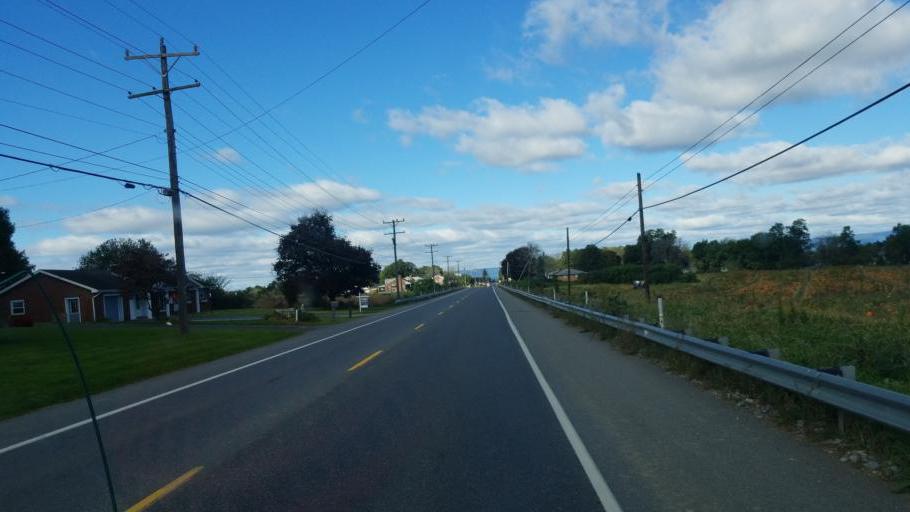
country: US
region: Pennsylvania
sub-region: Franklin County
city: Greencastle
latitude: 39.7836
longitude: -77.6970
